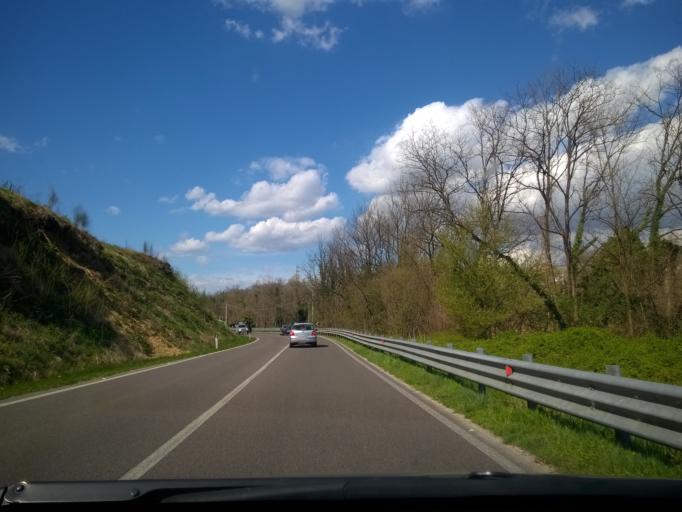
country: IT
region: Veneto
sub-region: Provincia di Treviso
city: San Pietro di Feletto
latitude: 45.8889
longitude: 12.2276
